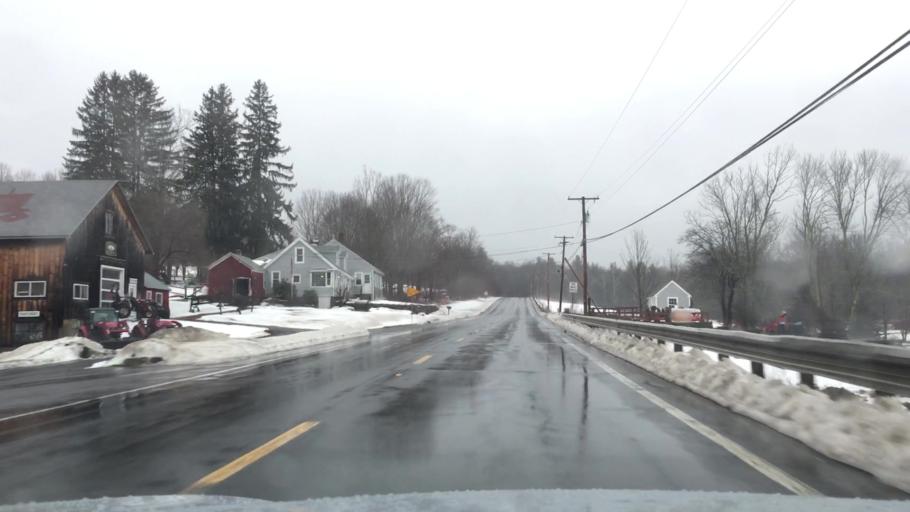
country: US
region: Massachusetts
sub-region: Hampshire County
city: Belchertown
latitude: 42.3107
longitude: -72.4065
